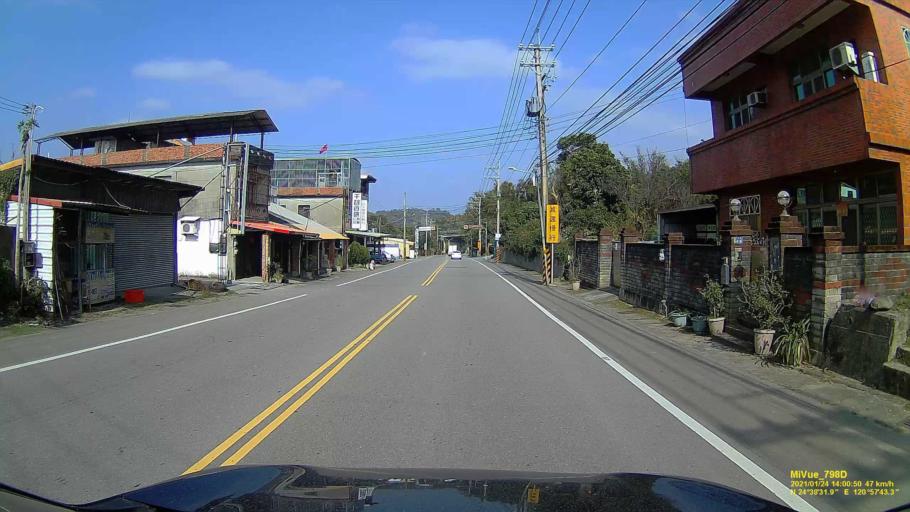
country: TW
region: Taiwan
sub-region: Hsinchu
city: Hsinchu
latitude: 24.6590
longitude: 120.9620
